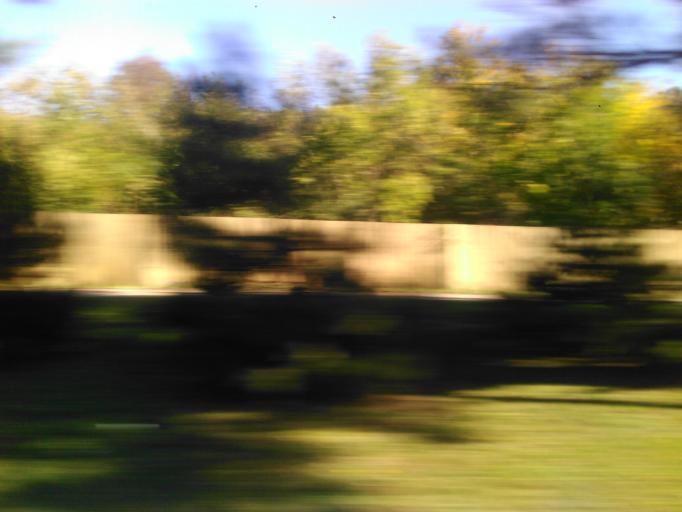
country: RU
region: Krasnodarskiy
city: Gelendzhik
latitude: 44.5823
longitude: 38.0628
